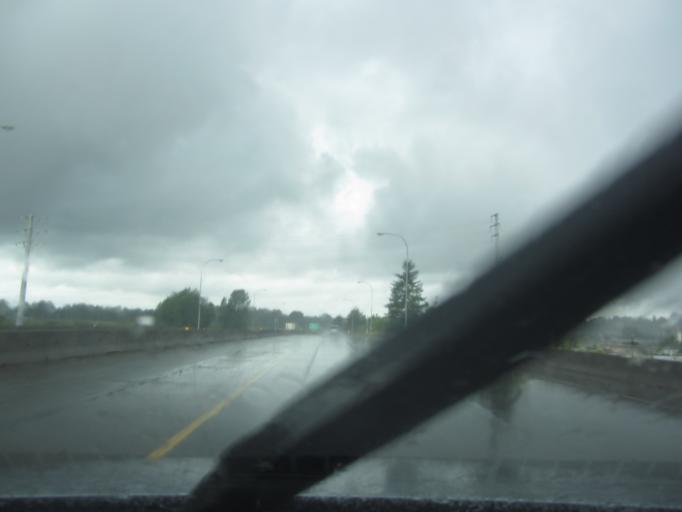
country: CA
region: British Columbia
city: Abbotsford
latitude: 49.1300
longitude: -122.3069
